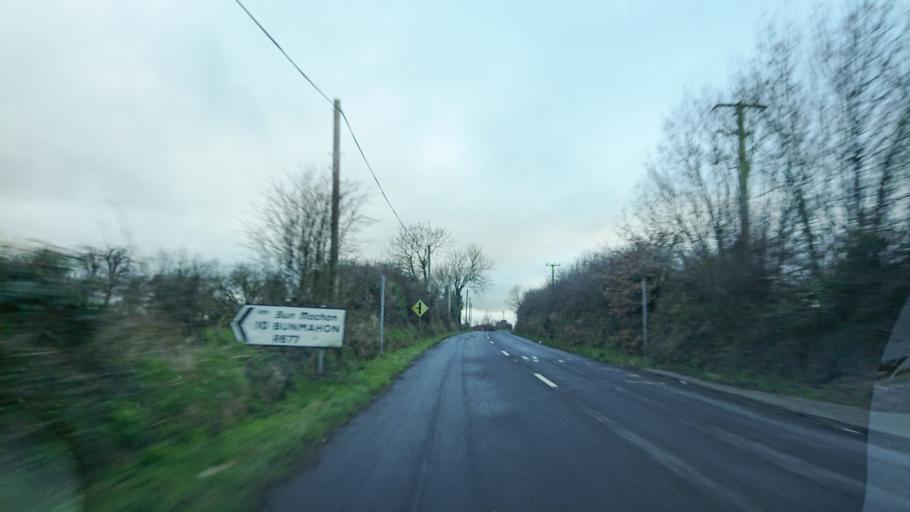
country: IE
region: Munster
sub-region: Waterford
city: Portlaw
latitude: 52.1999
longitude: -7.4260
